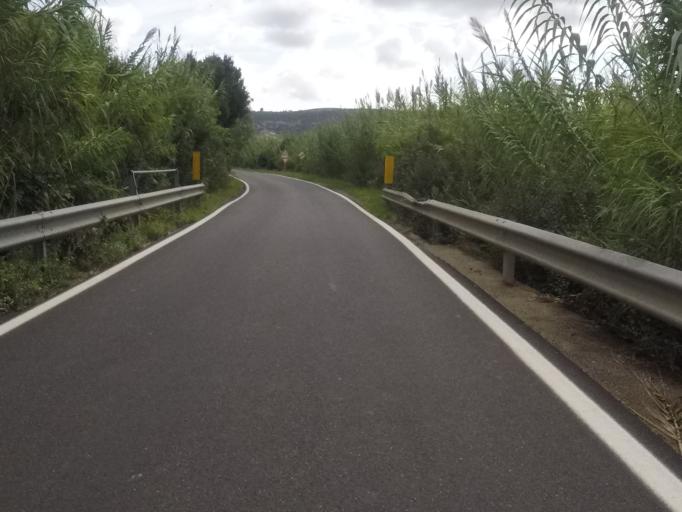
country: IT
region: Sardinia
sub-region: Provincia di Oristano
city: Bauladu
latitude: 40.0232
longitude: 8.6655
